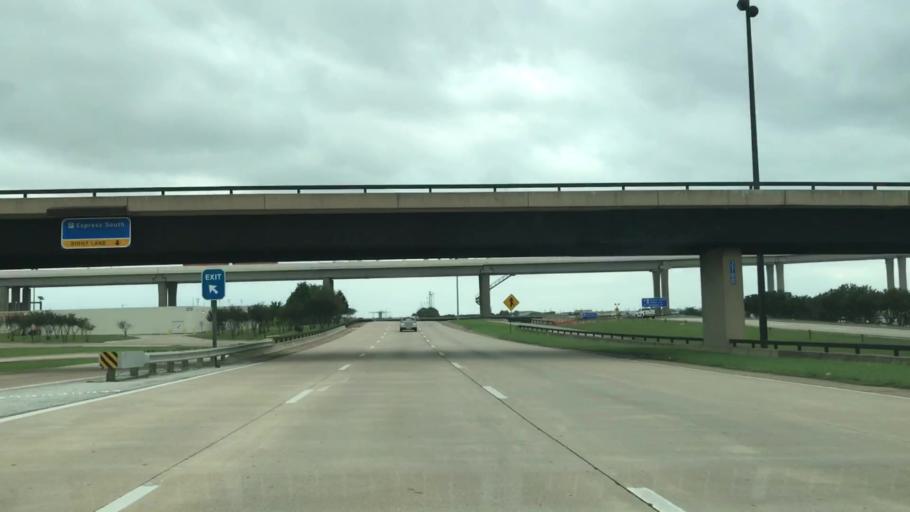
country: US
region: Texas
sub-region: Tarrant County
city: Grapevine
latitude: 32.8896
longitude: -97.0411
